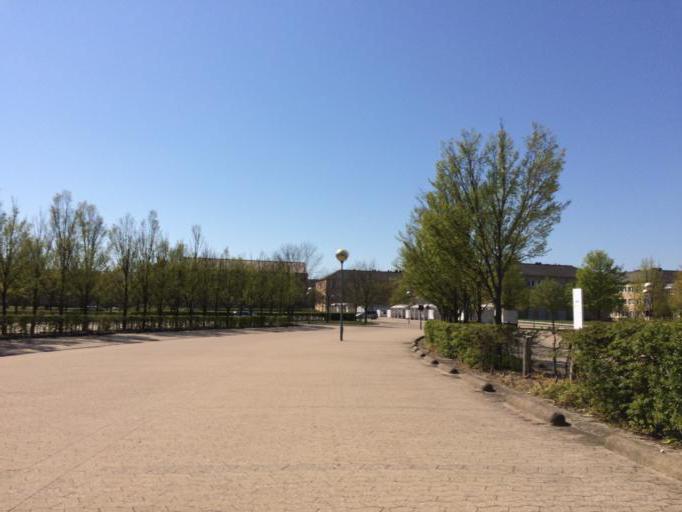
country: DK
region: Capital Region
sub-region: Hoje-Taastrup Kommune
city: Taastrup
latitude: 55.6477
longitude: 12.2800
